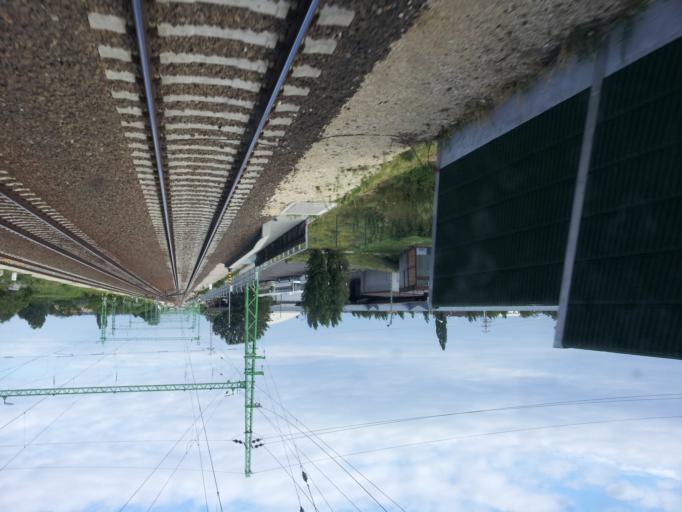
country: HU
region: Pest
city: Erd
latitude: 47.3698
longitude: 18.8843
